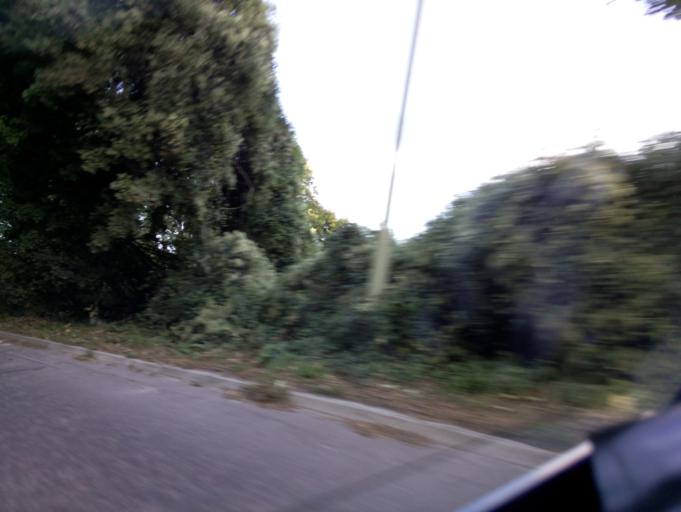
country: GB
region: England
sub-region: Hampshire
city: Basingstoke
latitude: 51.2844
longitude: -1.1106
